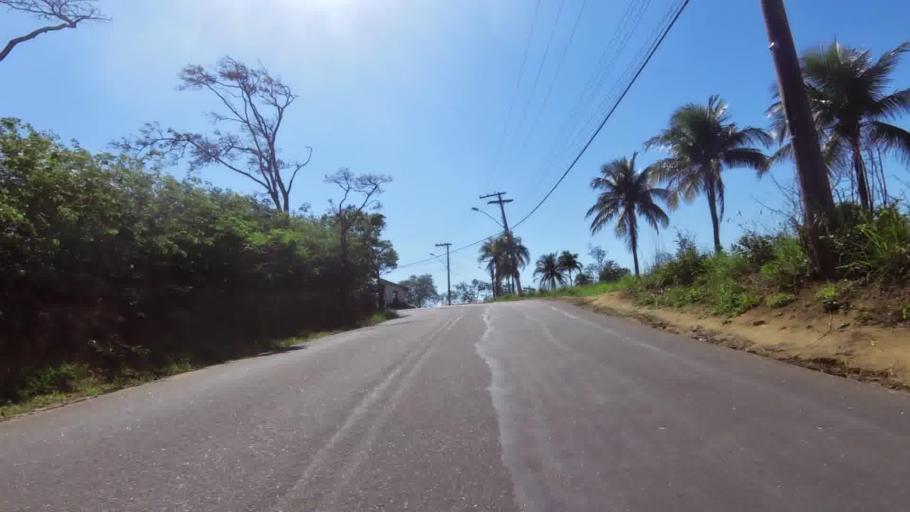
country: BR
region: Espirito Santo
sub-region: Guarapari
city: Guarapari
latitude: -20.7323
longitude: -40.5557
